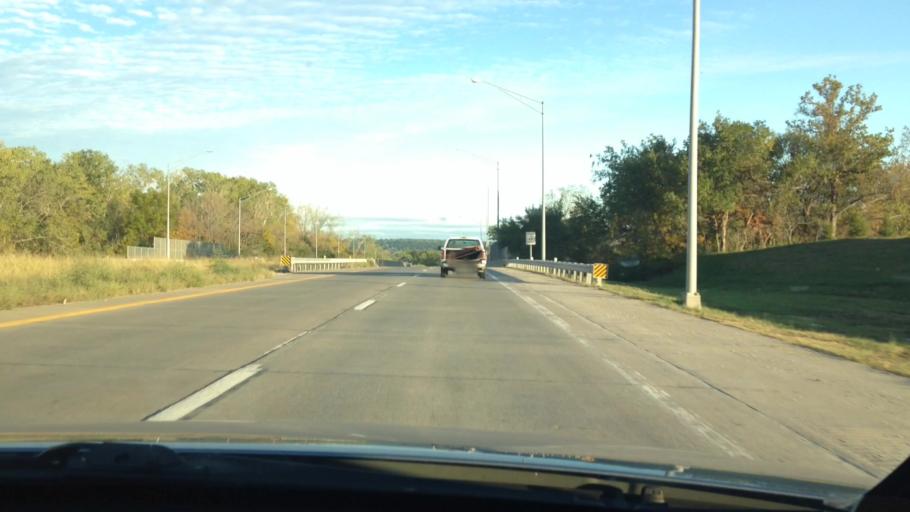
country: US
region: Missouri
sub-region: Clay County
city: Claycomo
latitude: 39.1593
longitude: -94.4897
